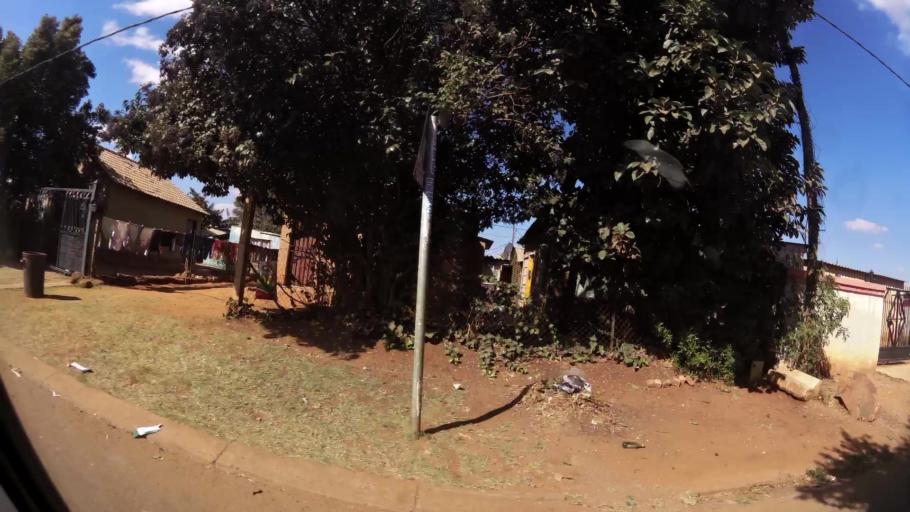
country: ZA
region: Gauteng
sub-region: City of Tshwane Metropolitan Municipality
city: Cullinan
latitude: -25.7170
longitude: 28.4034
